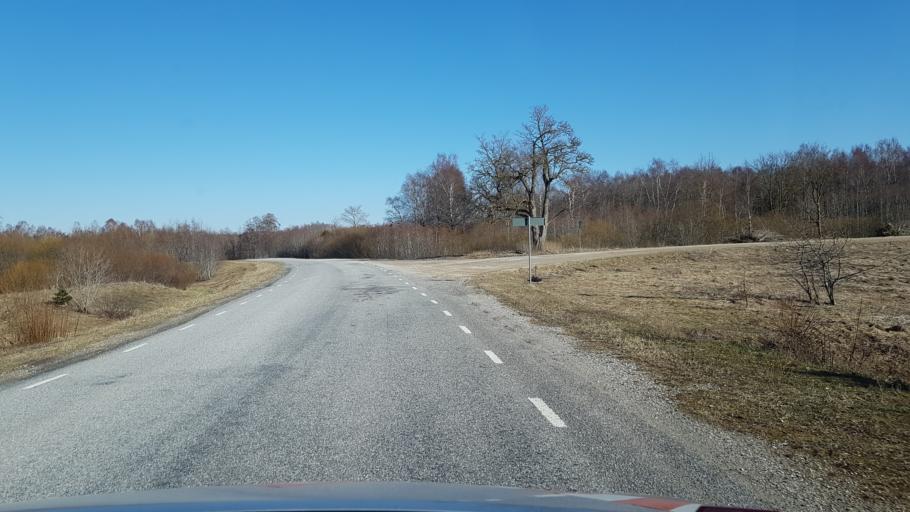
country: EE
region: Laeaene-Virumaa
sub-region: Kadrina vald
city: Kadrina
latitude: 59.3444
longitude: 26.0827
